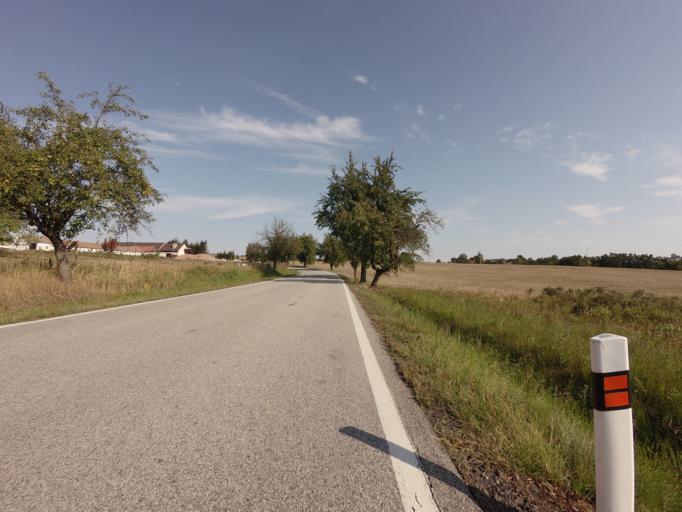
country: CZ
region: Jihocesky
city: Tyn nad Vltavou
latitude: 49.2756
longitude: 14.4018
